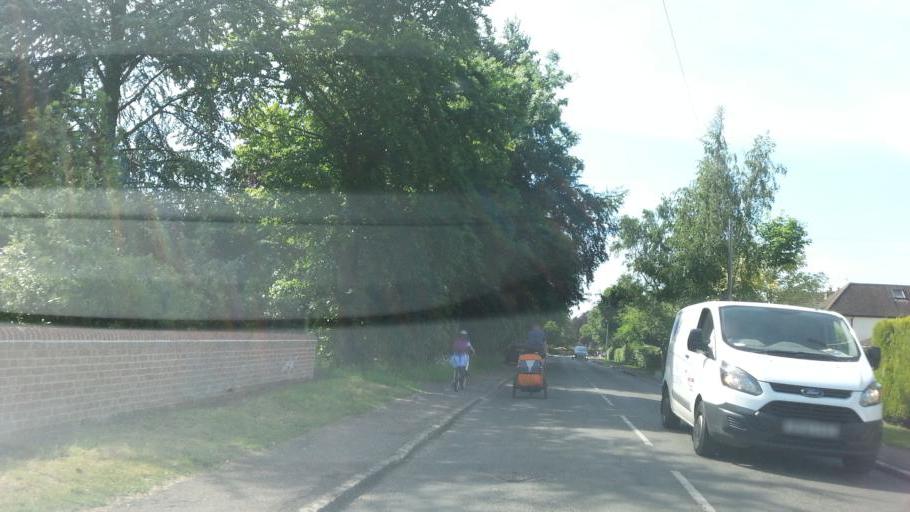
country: GB
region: England
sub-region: Cambridgeshire
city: Sawston
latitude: 52.1485
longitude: 0.1449
